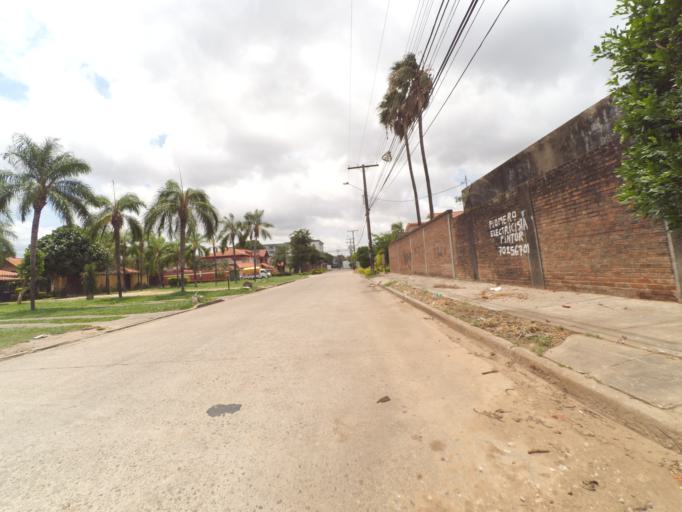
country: BO
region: Santa Cruz
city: Santa Cruz de la Sierra
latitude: -17.7863
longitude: -63.2009
